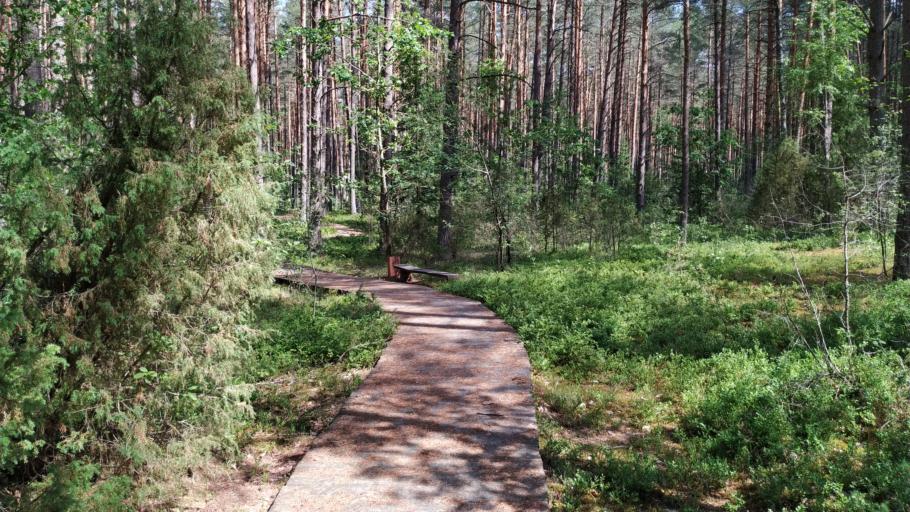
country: LT
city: Nemencine
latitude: 54.8082
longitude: 25.3975
